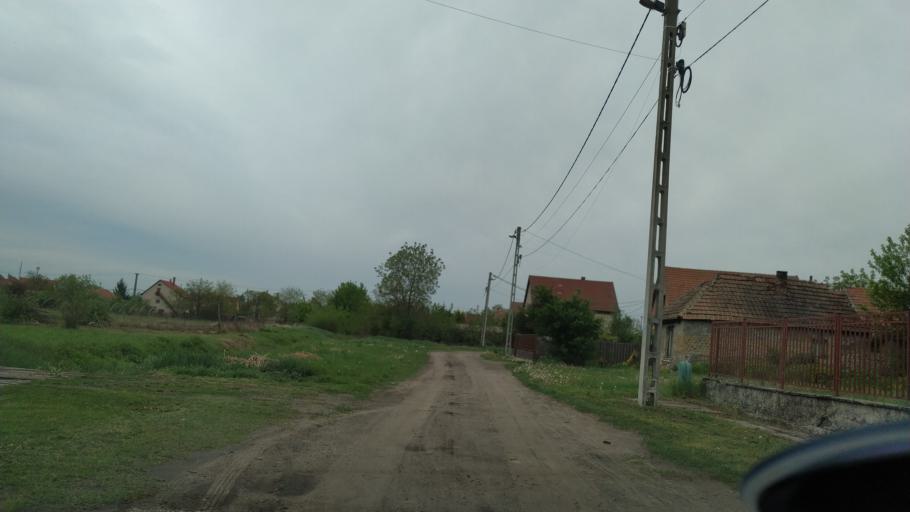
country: HU
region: Pest
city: Nagykata
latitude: 47.4119
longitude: 19.7290
